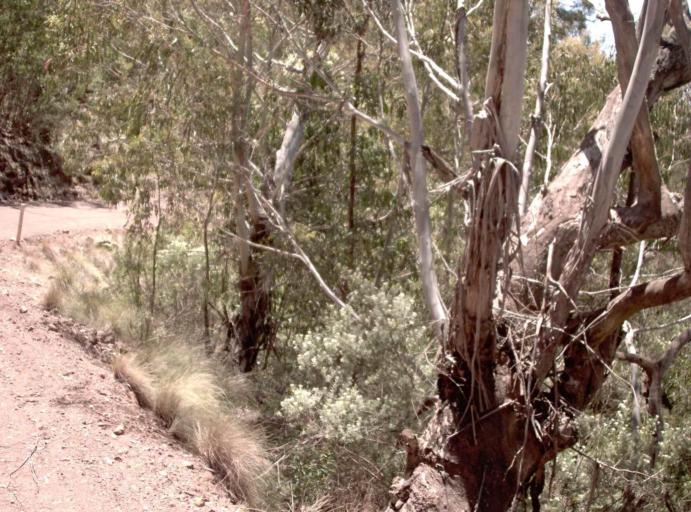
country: AU
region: New South Wales
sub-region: Snowy River
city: Jindabyne
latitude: -37.0013
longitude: 148.2953
